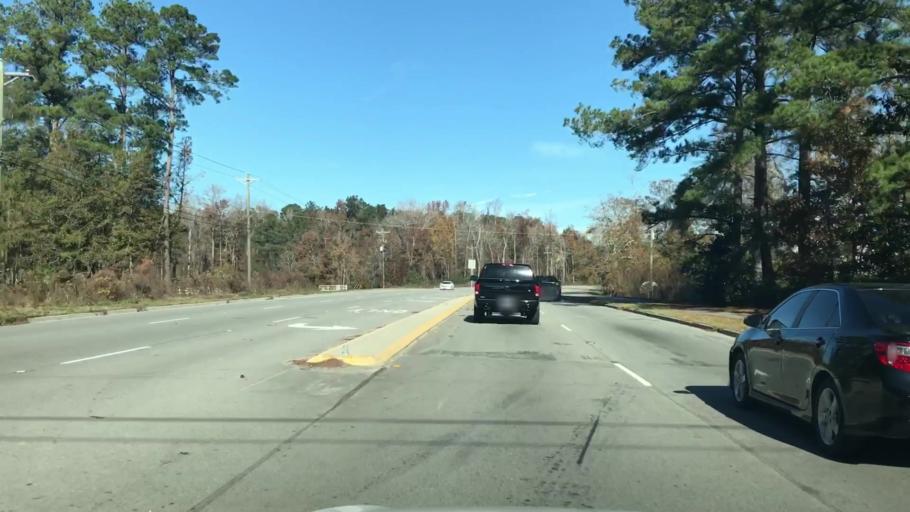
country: US
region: South Carolina
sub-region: Dorchester County
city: Centerville
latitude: 32.9631
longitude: -80.2017
